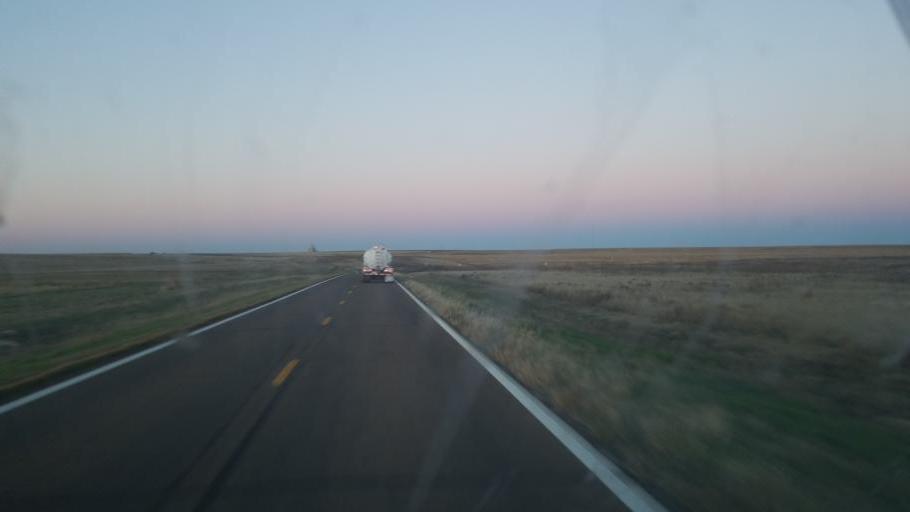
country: US
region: Kansas
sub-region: Wallace County
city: Sharon Springs
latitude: 38.9269
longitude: -101.5564
